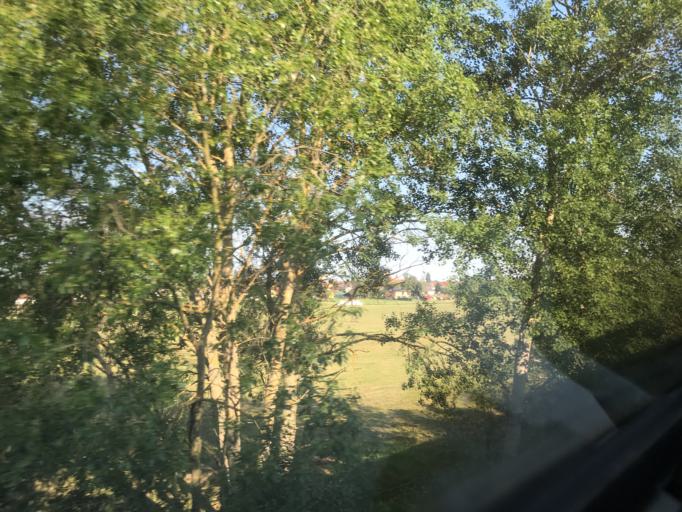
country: CZ
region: Jihocesky
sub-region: Okres Jindrichuv Hradec
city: Lomnice nad Luznici
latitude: 49.0781
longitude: 14.7262
